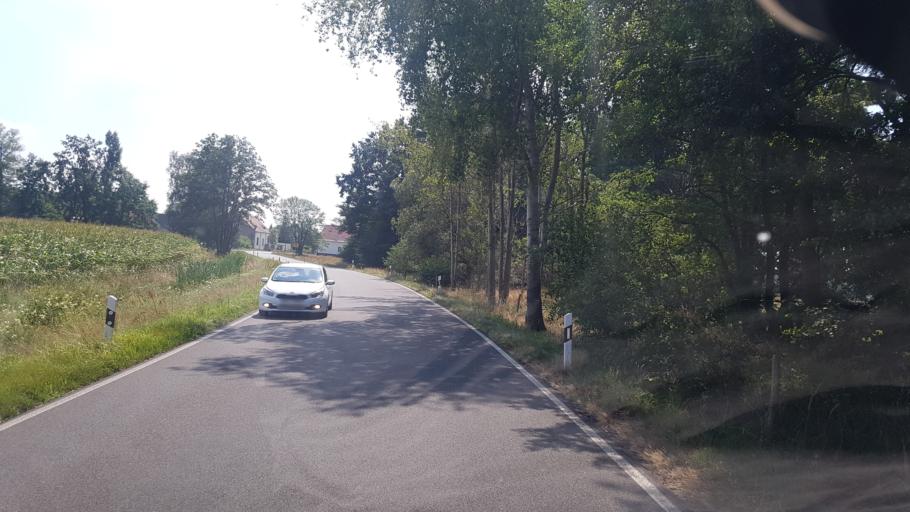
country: DE
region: Brandenburg
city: Cottbus
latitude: 51.7013
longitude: 14.4263
